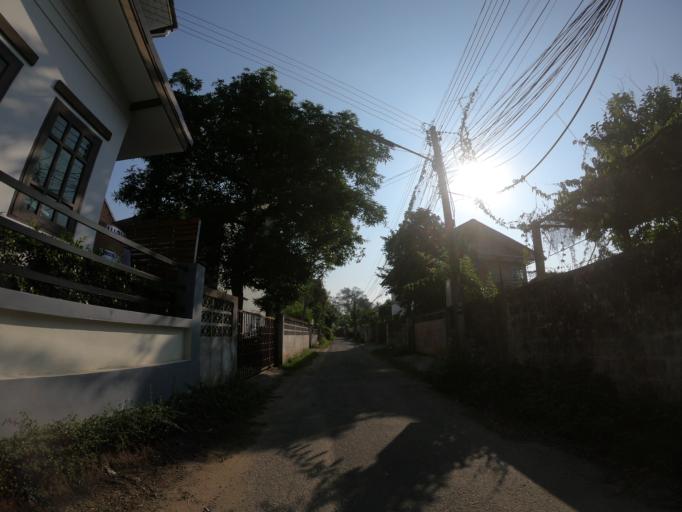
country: TH
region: Chiang Mai
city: Chiang Mai
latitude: 18.8020
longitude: 99.0059
